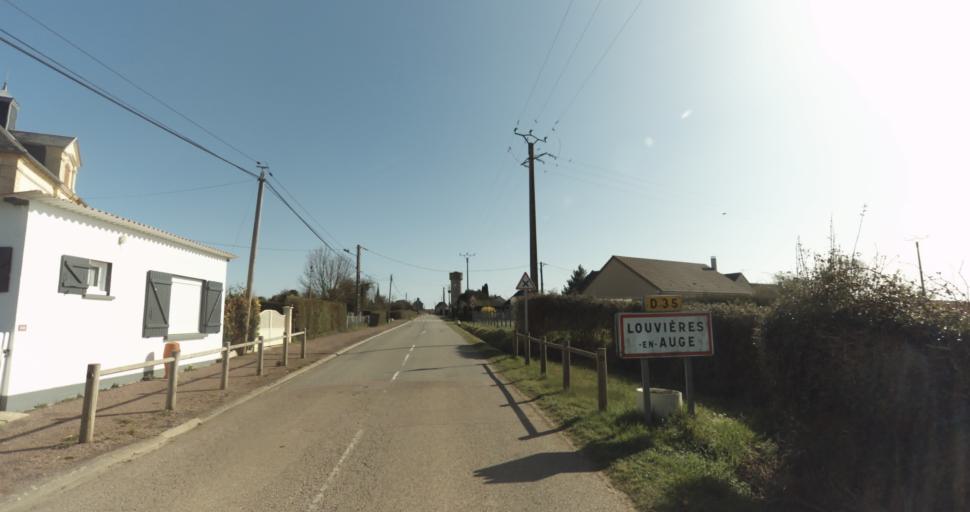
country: FR
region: Lower Normandy
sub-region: Departement de l'Orne
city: Trun
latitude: 48.8727
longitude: 0.0296
